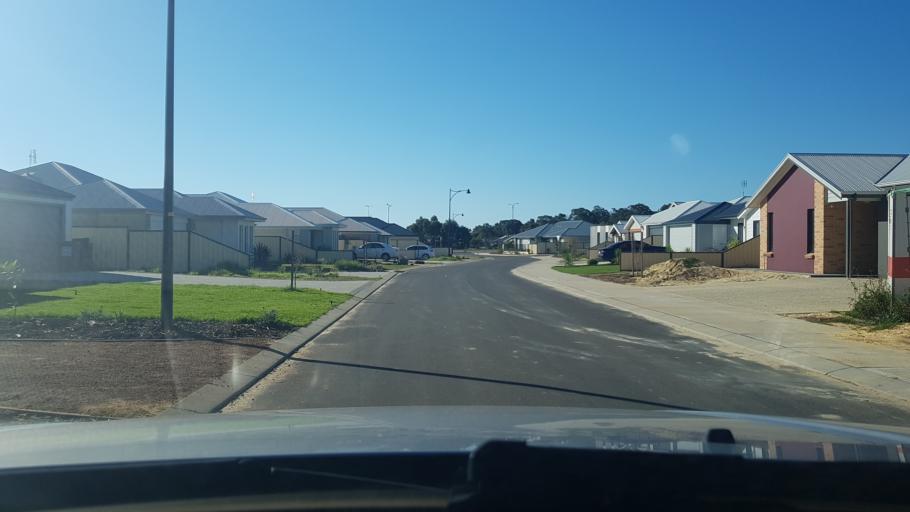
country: AU
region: Western Australia
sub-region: Augusta-Margaret River Shire
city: Margaret River
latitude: -33.8571
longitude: 115.1009
